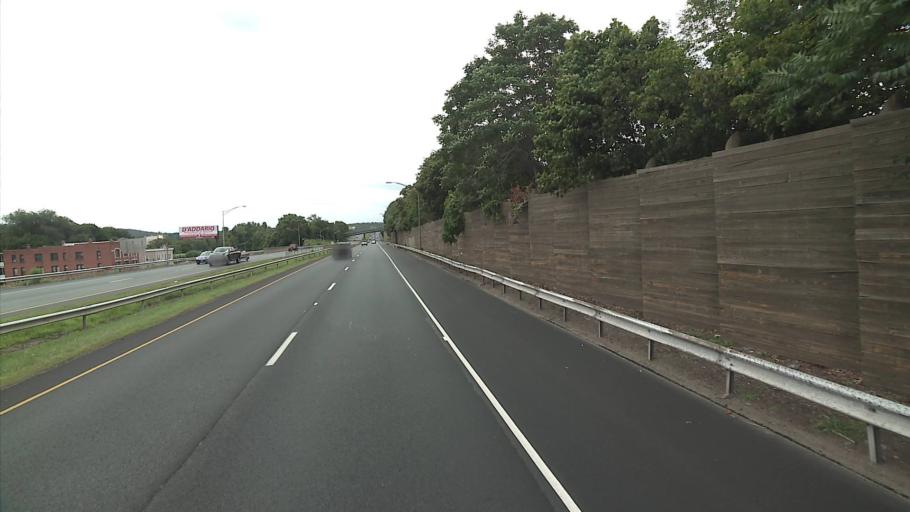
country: US
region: Connecticut
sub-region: New Haven County
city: Waterbury
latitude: 41.5412
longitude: -73.0447
